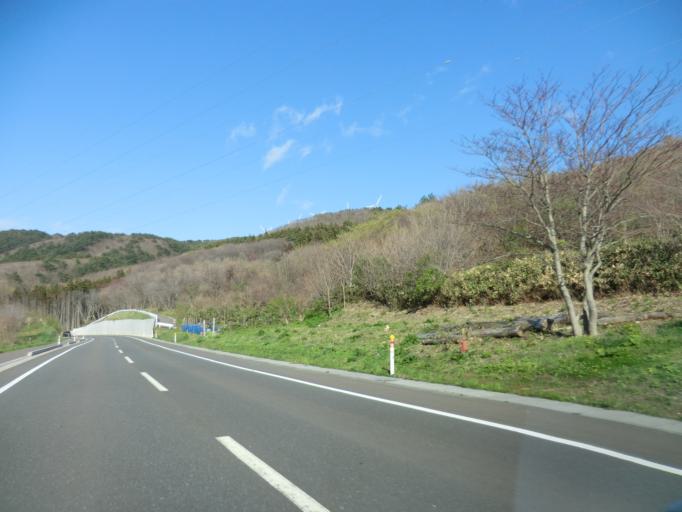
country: JP
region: Aomori
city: Mutsu
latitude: 41.3842
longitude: 141.4079
